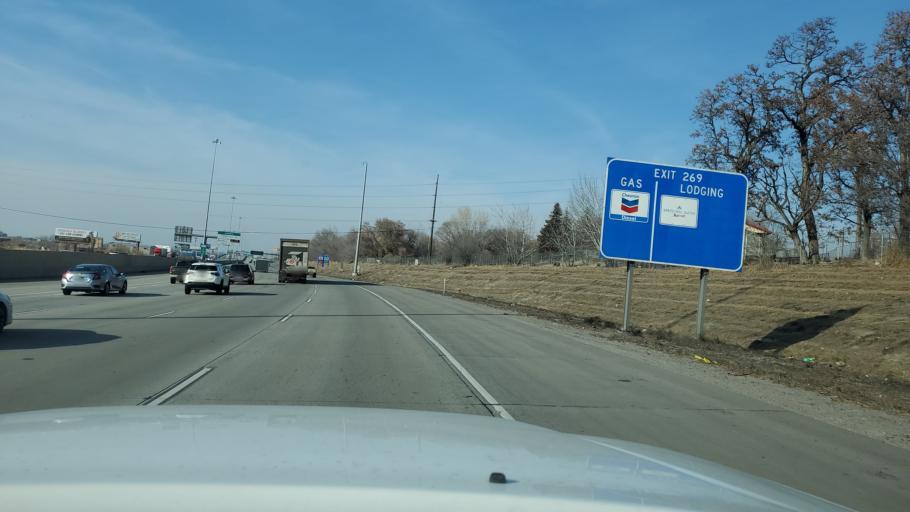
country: US
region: Utah
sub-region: Utah County
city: Provo
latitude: 40.2525
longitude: -111.6961
